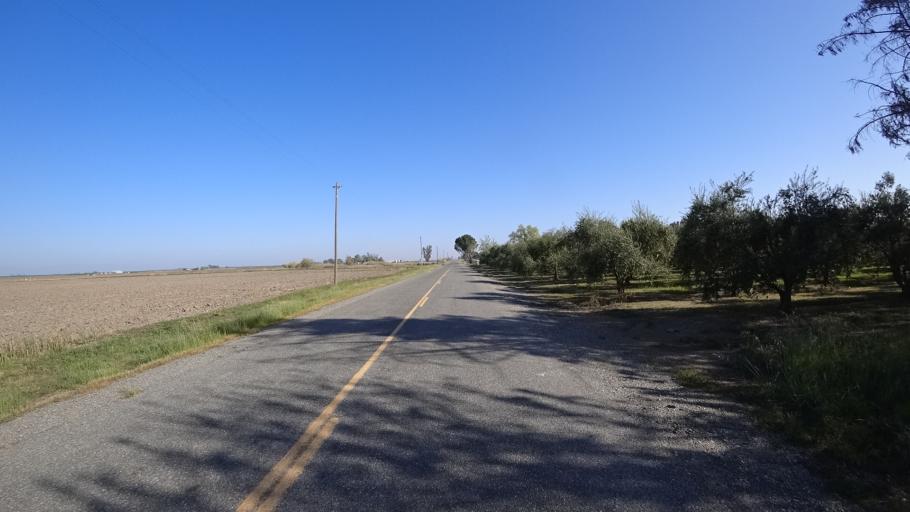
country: US
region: California
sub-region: Glenn County
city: Willows
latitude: 39.5610
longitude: -122.1077
